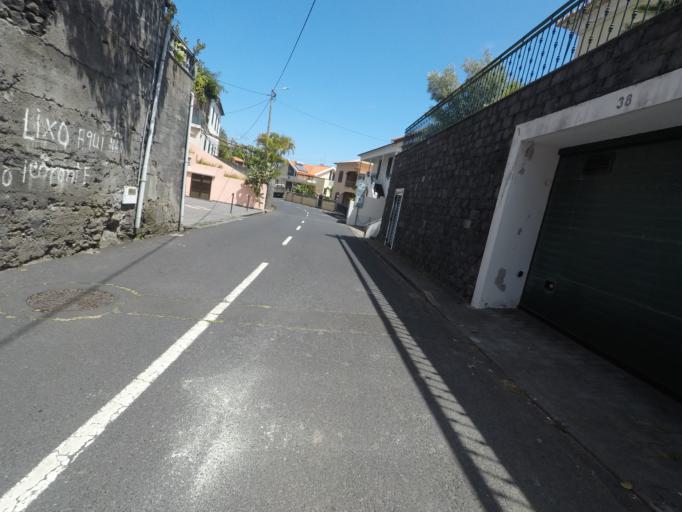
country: PT
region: Madeira
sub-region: Porto Moniz
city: Porto Moniz
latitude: 32.8239
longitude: -17.1064
